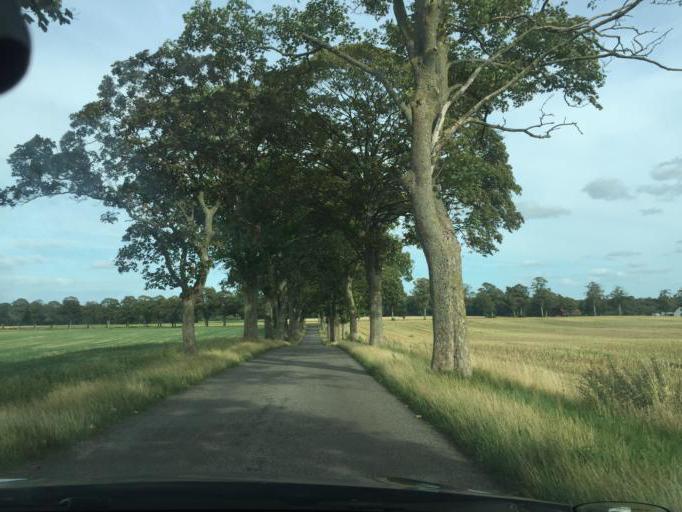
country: DK
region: South Denmark
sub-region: Kerteminde Kommune
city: Langeskov
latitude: 55.3534
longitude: 10.5390
